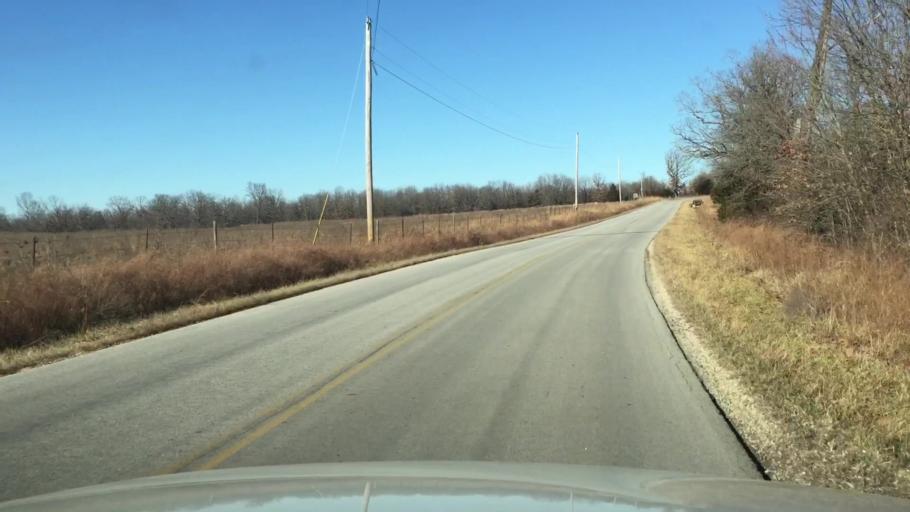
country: US
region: Missouri
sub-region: Morgan County
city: Versailles
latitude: 38.3466
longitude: -92.7490
